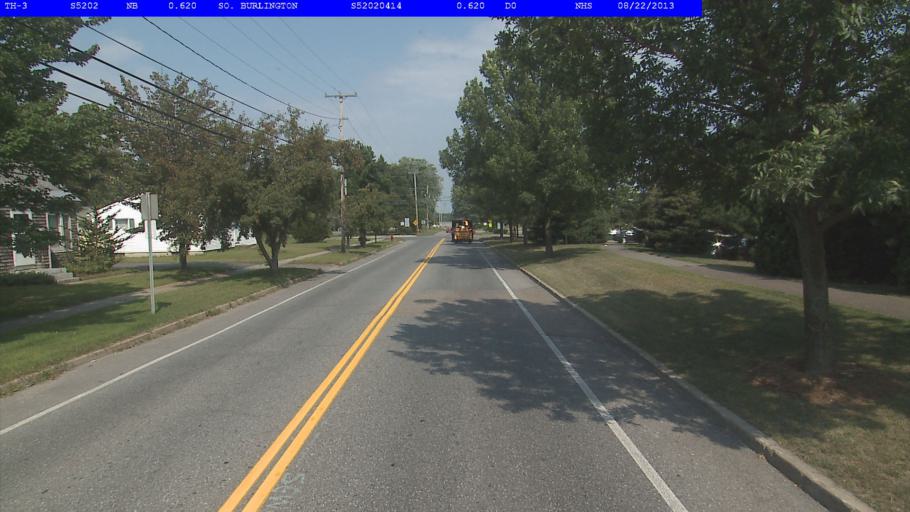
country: US
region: Vermont
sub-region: Chittenden County
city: South Burlington
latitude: 44.4716
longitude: -73.1580
